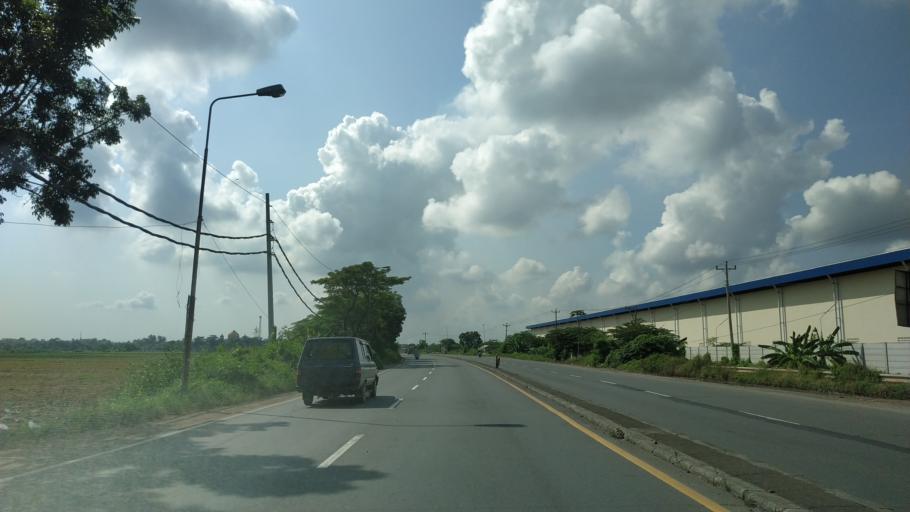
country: ID
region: Central Java
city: Wiradesa
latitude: -6.8879
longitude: 109.5764
